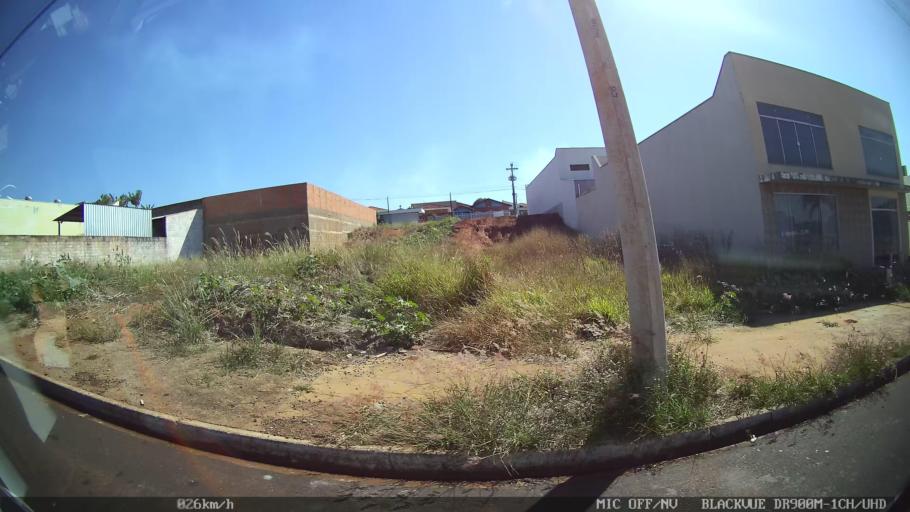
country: BR
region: Sao Paulo
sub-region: Batatais
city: Batatais
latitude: -20.8840
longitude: -47.5980
